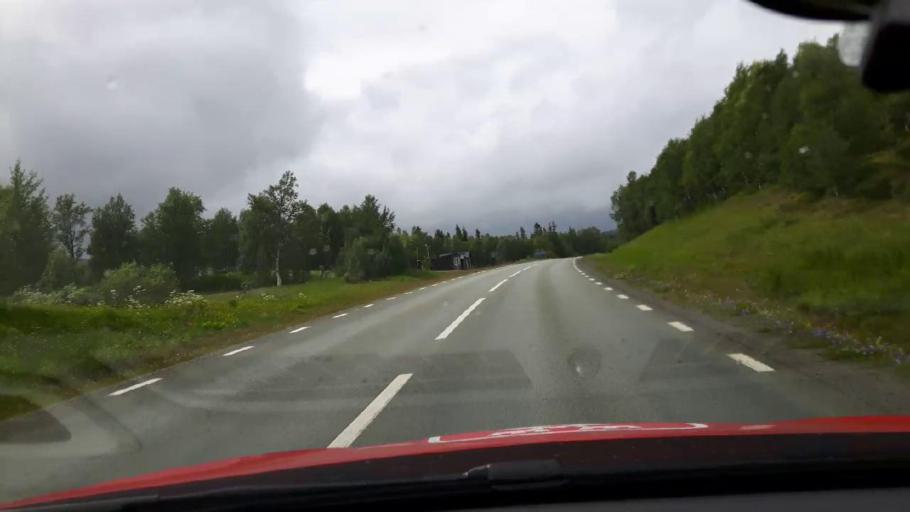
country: NO
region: Nord-Trondelag
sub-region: Meraker
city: Meraker
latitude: 63.2826
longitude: 12.1292
